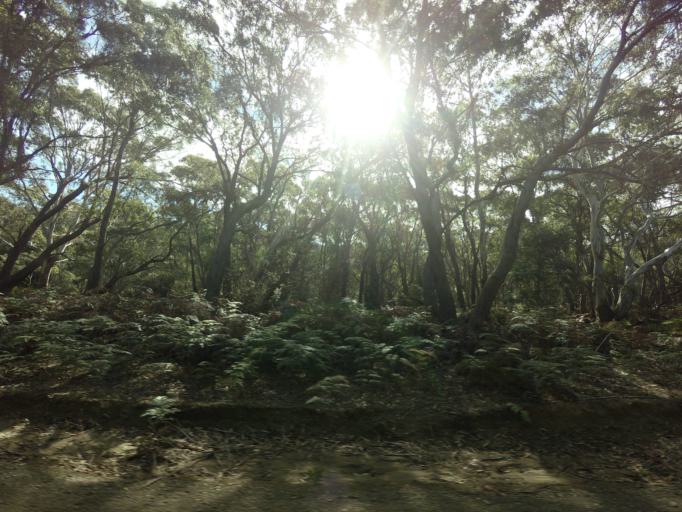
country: AU
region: Tasmania
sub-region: Clarence
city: Sandford
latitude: -43.0838
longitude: 147.6823
